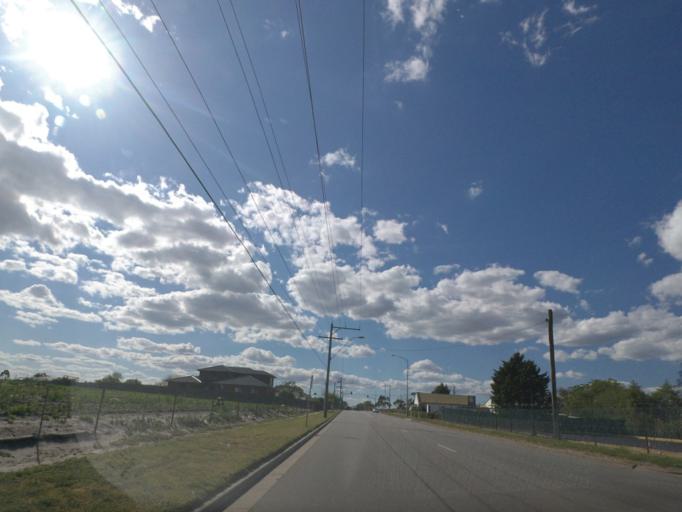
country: AU
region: Victoria
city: Heatherton
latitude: -37.9574
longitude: 145.1006
